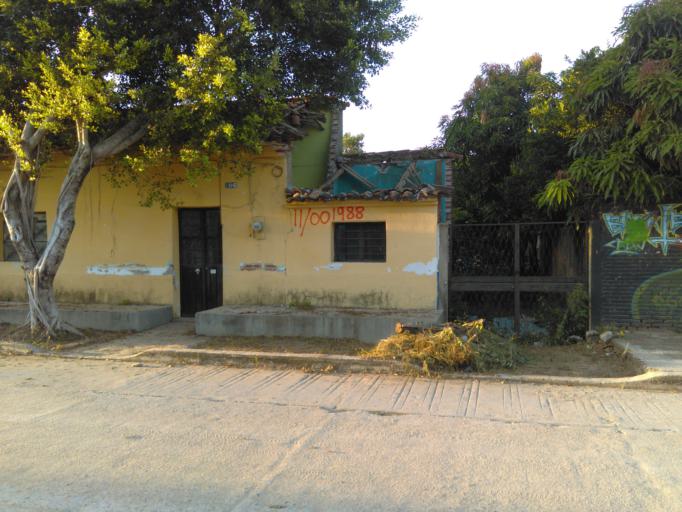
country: MX
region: Oaxaca
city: San Jeronimo Ixtepec
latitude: 16.5683
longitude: -95.1040
